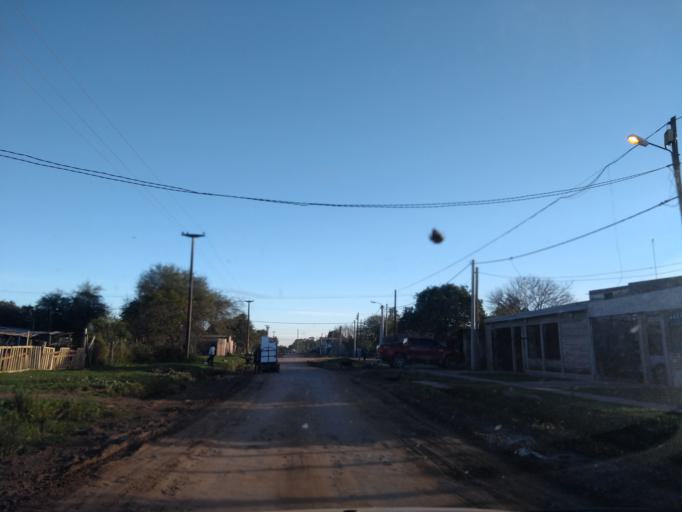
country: AR
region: Chaco
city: Puerto Vilelas
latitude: -27.5003
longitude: -58.9699
